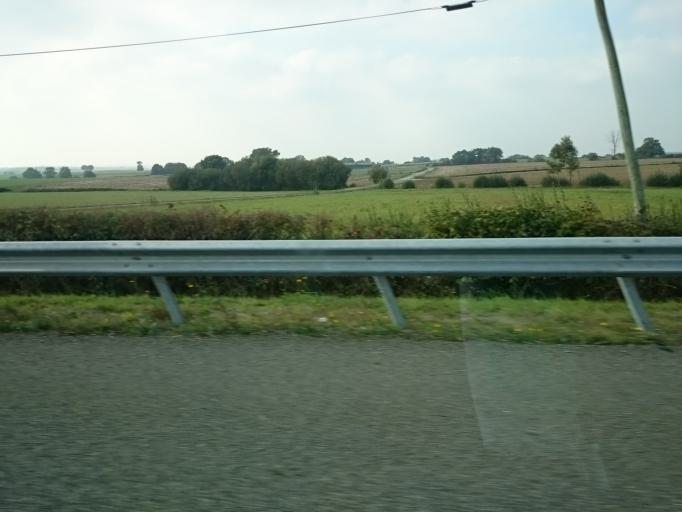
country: FR
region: Brittany
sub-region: Departement d'Ille-et-Vilaine
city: Crevin
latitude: 47.9045
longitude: -1.6855
